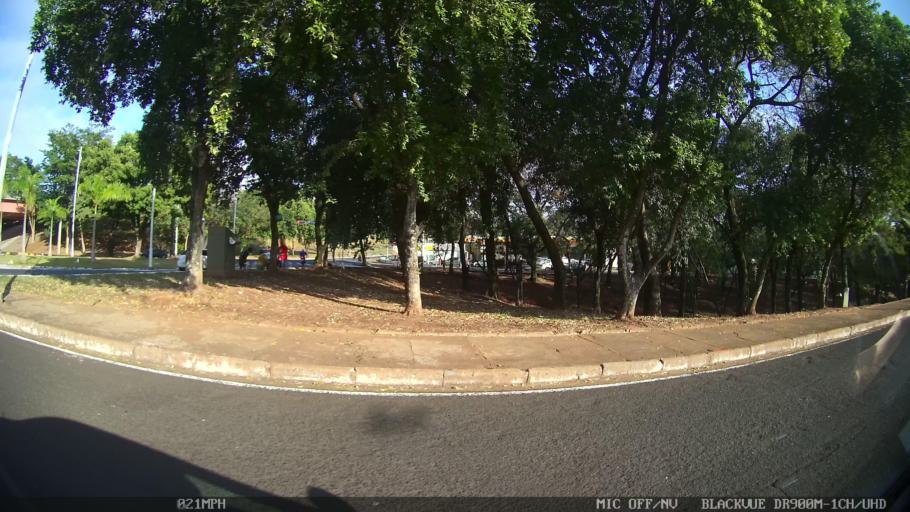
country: BR
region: Sao Paulo
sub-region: Sao Jose Do Rio Preto
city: Sao Jose do Rio Preto
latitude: -20.8249
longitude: -49.3659
